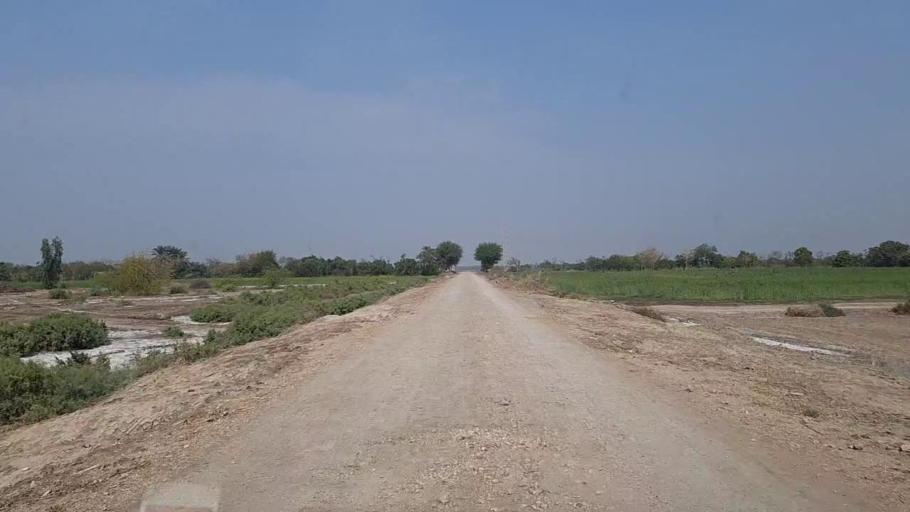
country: PK
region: Sindh
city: Mirwah Gorchani
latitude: 25.3263
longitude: 69.0615
